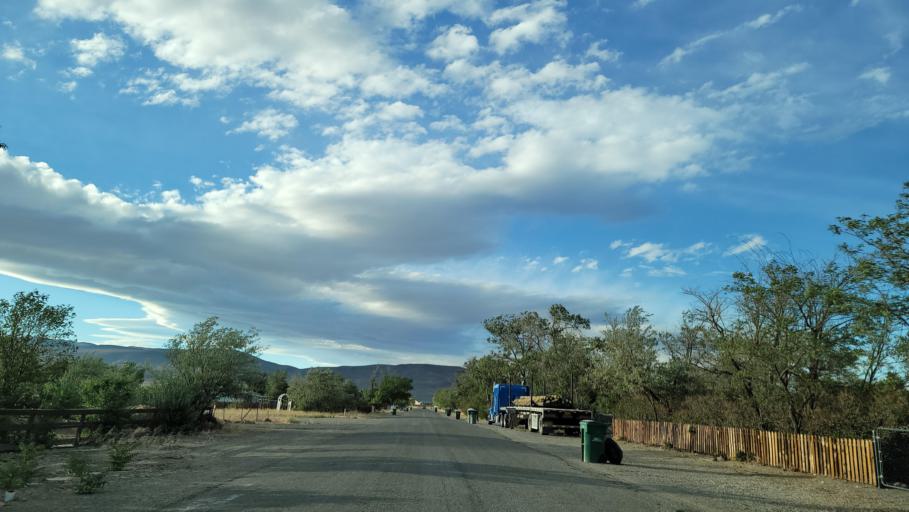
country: US
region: Nevada
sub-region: Lyon County
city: Silver Springs
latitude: 39.3948
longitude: -119.2374
